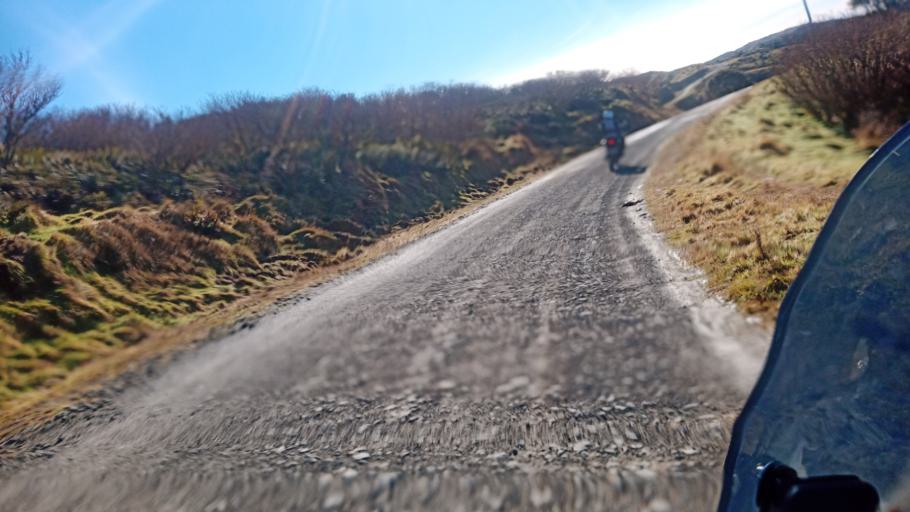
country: NZ
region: Gisborne
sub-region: Gisborne District
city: Gisborne
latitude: -38.1834
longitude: 177.8217
